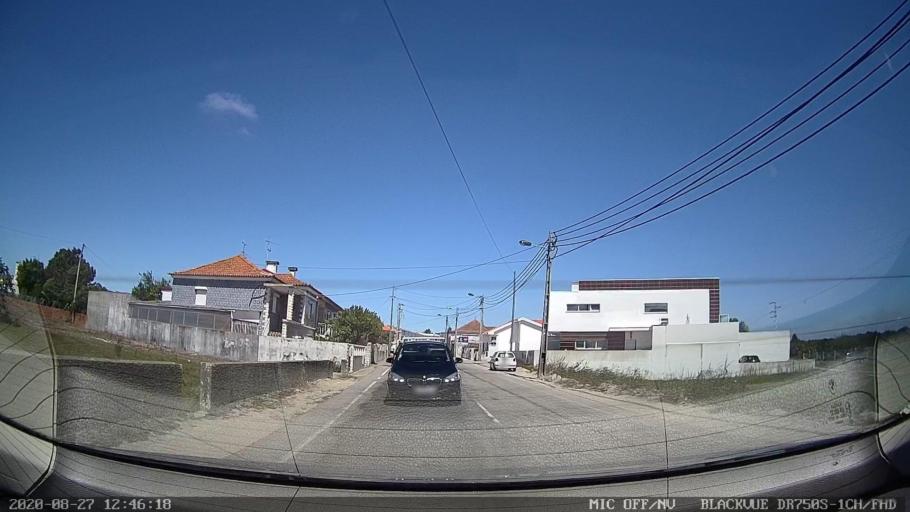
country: PT
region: Aveiro
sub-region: Ilhavo
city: Ilhavo
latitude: 40.6135
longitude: -8.6839
